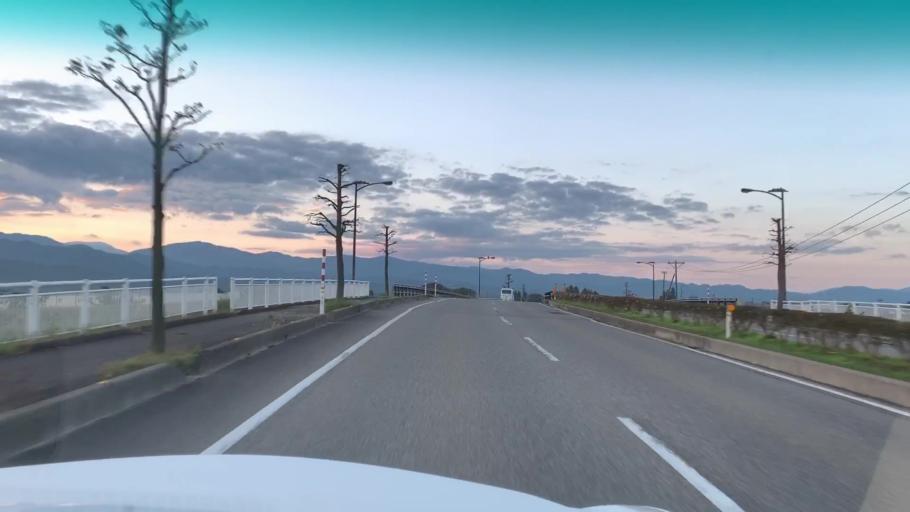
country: JP
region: Toyama
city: Kamiichi
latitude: 36.6951
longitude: 137.3429
